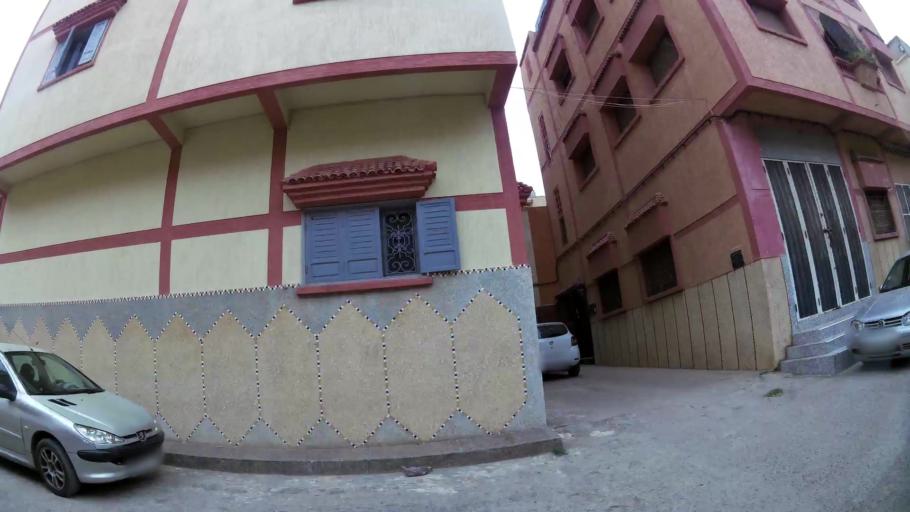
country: MA
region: Rabat-Sale-Zemmour-Zaer
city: Sale
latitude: 34.0420
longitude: -6.8079
